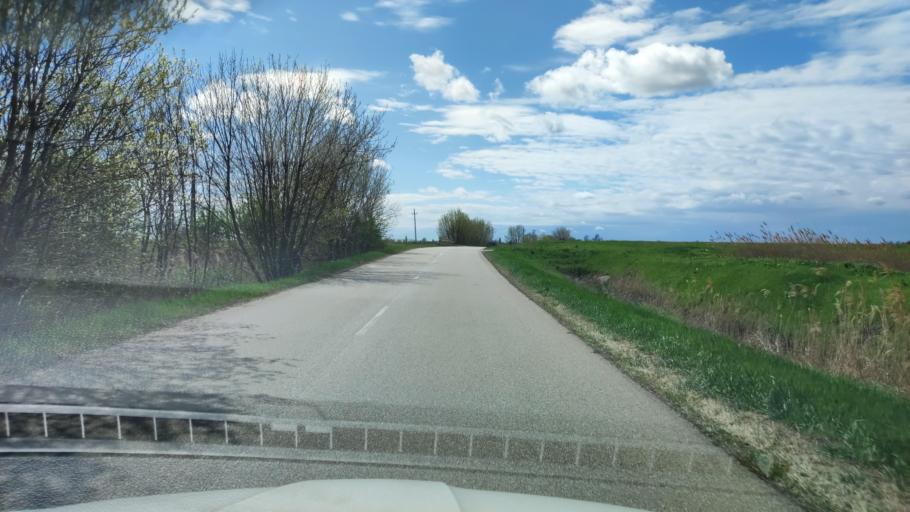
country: HU
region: Pest
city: Abony
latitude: 47.1315
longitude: 20.0140
